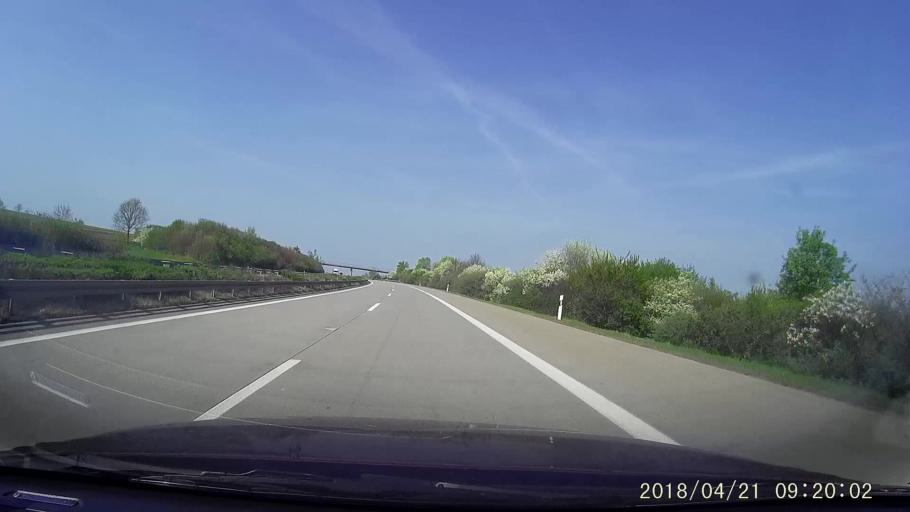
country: DE
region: Saxony
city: Weissenberg
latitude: 51.2108
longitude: 14.6258
